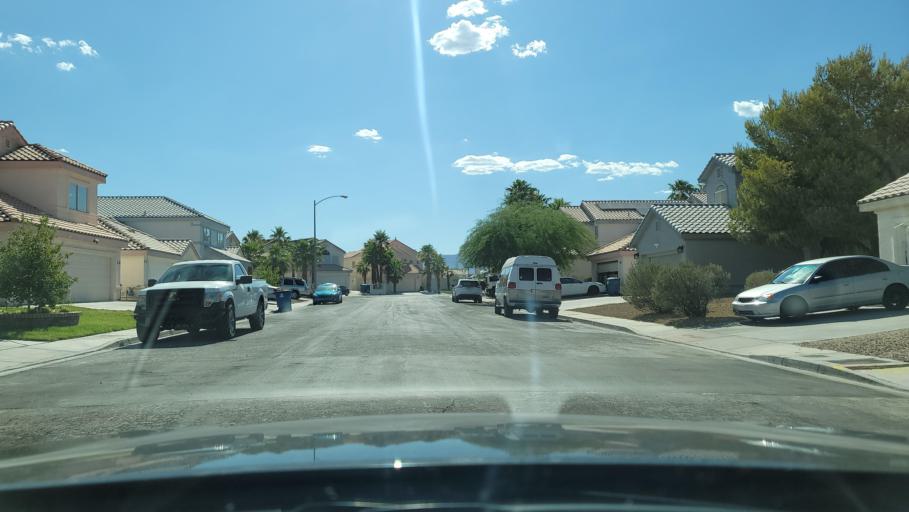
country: US
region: Nevada
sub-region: Clark County
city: Spring Valley
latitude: 36.0898
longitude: -115.2494
